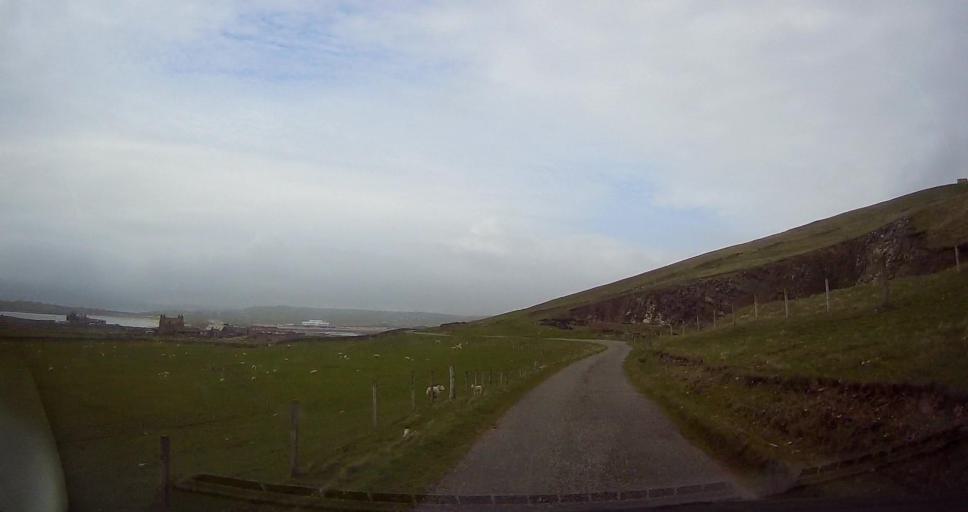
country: GB
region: Scotland
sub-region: Shetland Islands
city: Sandwick
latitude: 59.8649
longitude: -1.2779
